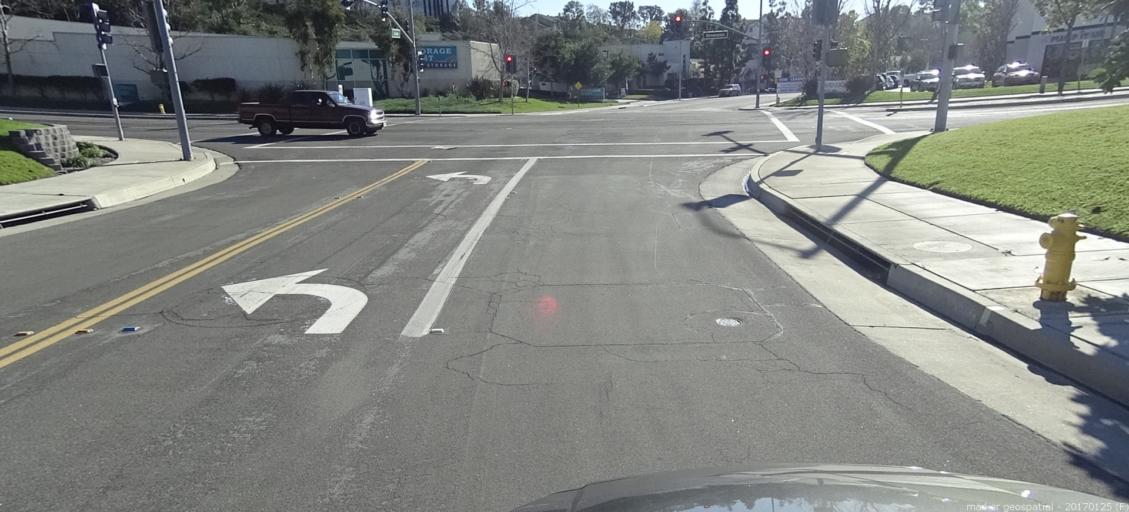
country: US
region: California
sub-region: Orange County
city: Lake Forest
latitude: 33.6618
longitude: -117.6713
